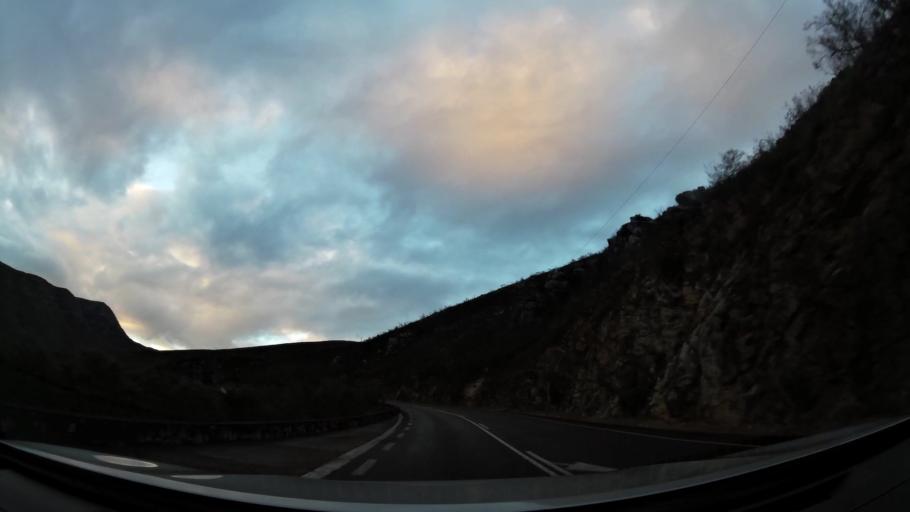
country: ZA
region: Western Cape
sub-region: Overberg District Municipality
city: Swellendam
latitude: -33.9854
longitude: 20.7102
